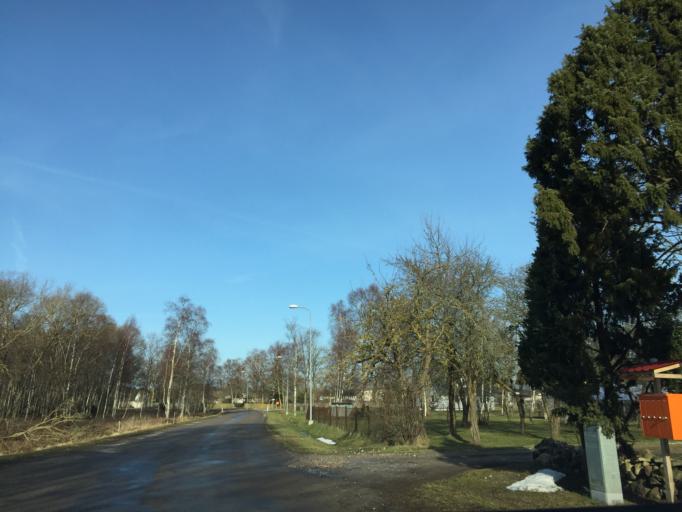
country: EE
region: Saare
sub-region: Kuressaare linn
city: Kuressaare
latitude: 58.3646
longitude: 22.0344
